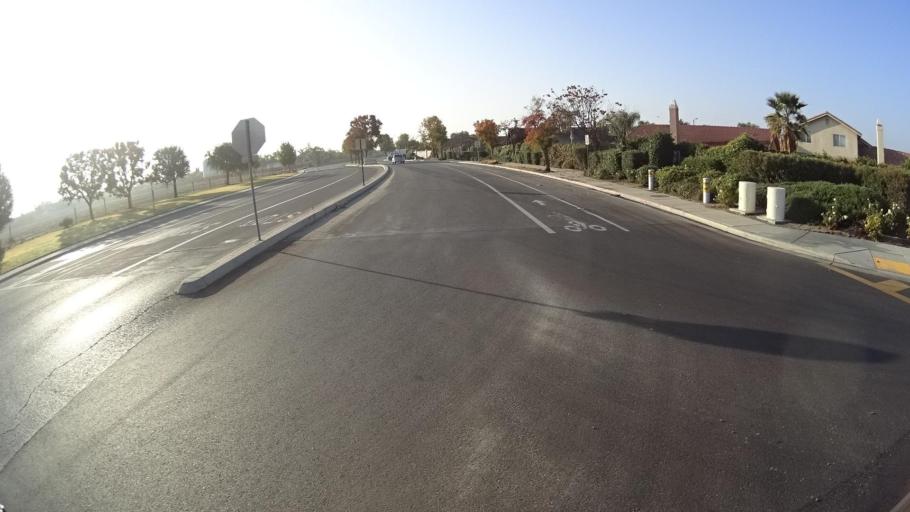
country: US
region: California
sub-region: Kern County
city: Delano
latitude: 35.7904
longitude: -119.2237
